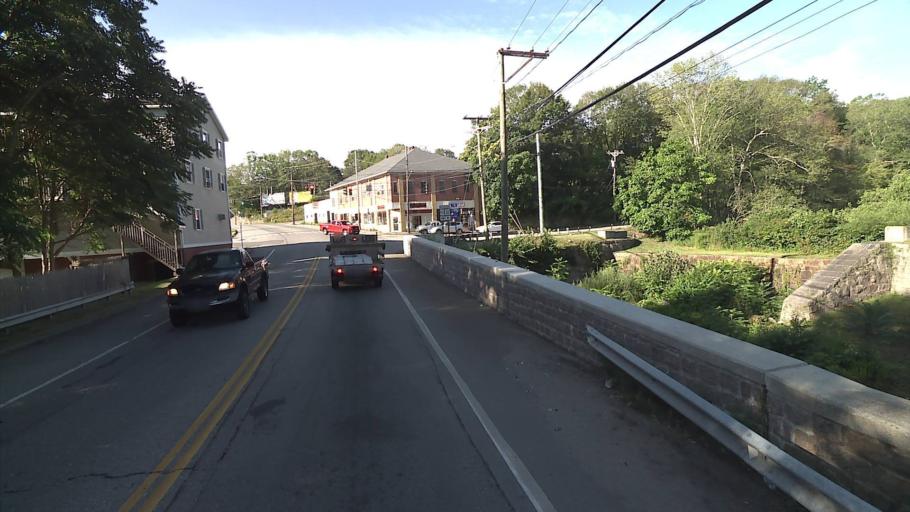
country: US
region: Connecticut
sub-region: New London County
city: Uncasville
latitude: 41.4370
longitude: -72.1095
